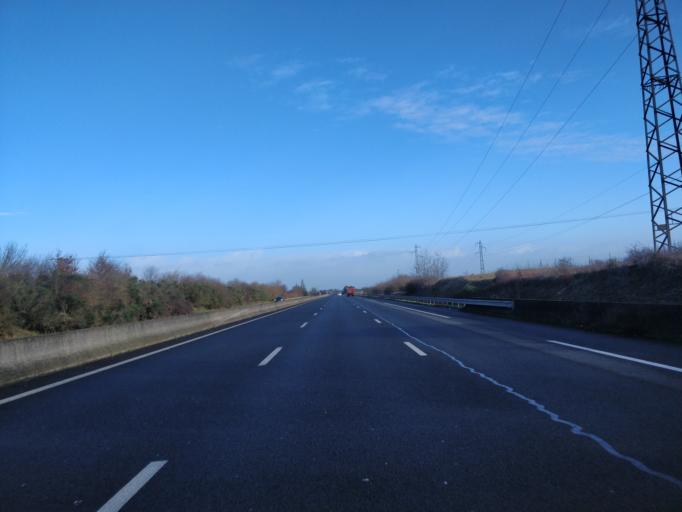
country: FR
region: Centre
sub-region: Departement du Loiret
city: Beaugency
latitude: 47.7943
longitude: 1.6078
